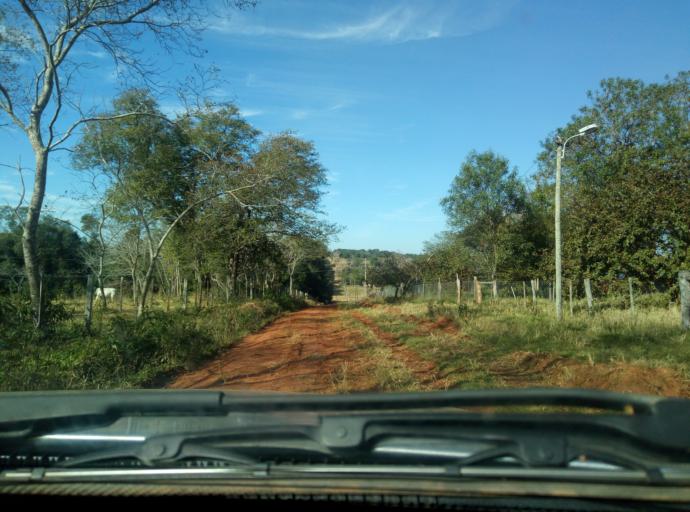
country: PY
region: Caaguazu
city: Carayao
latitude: -25.1710
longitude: -56.2943
